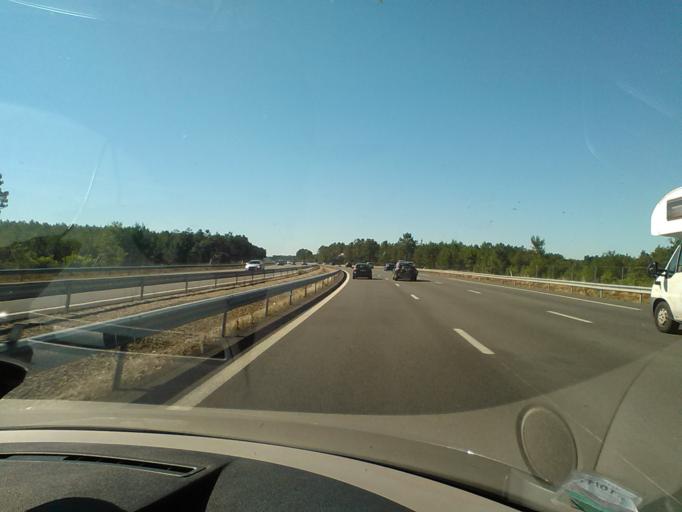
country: FR
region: Aquitaine
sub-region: Departement de la Gironde
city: Belin-Beliet
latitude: 44.4191
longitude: -0.8205
